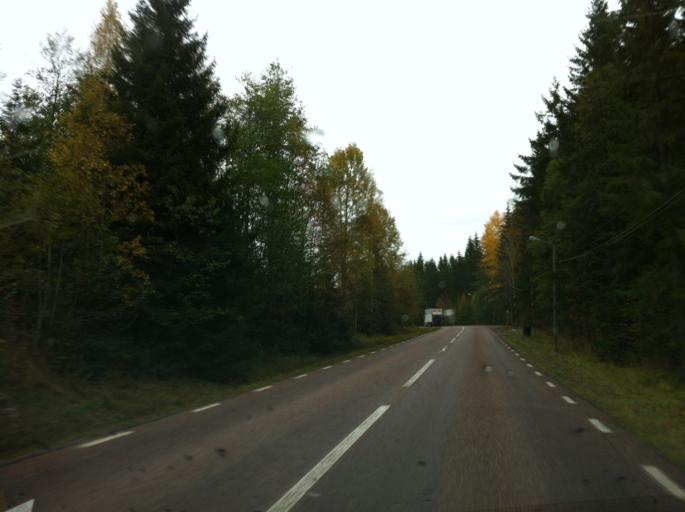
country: SE
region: Dalarna
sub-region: Ludvika Kommun
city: Grangesberg
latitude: 60.1623
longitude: 14.9718
